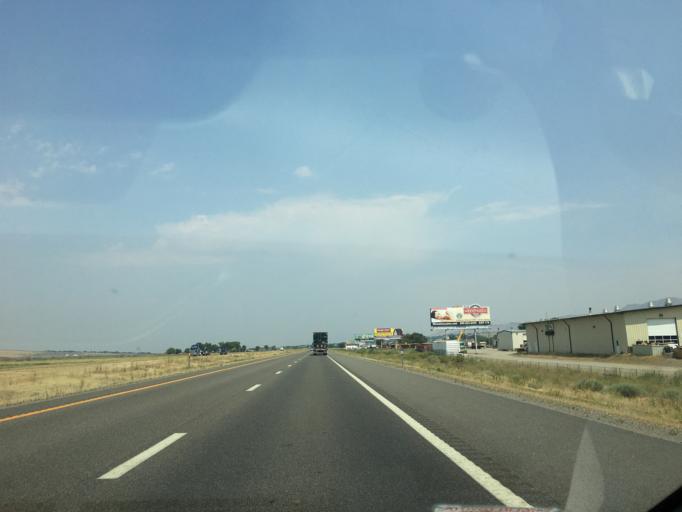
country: US
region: Nevada
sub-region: Humboldt County
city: Winnemucca
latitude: 40.9373
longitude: -117.7875
